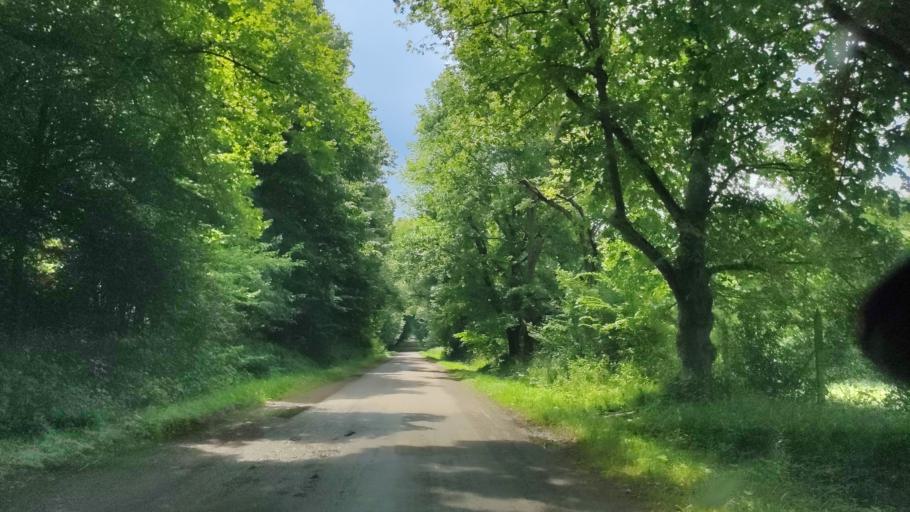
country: HU
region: Heves
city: Parad
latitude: 47.9142
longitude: 20.0584
